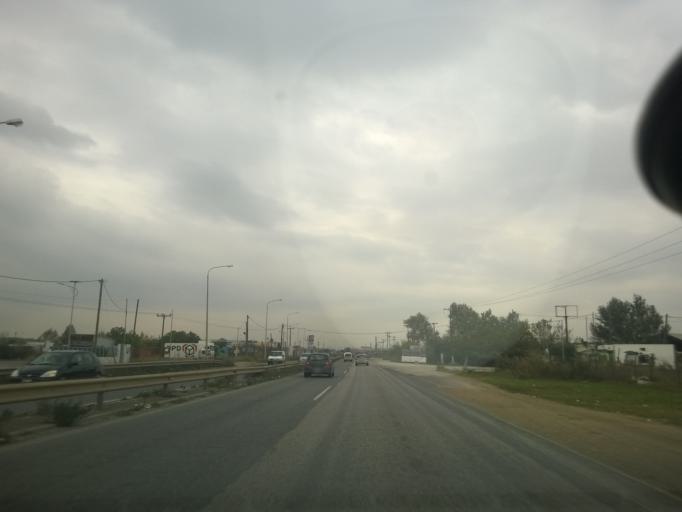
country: GR
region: Central Macedonia
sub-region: Nomos Thessalonikis
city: Sindos
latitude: 40.7059
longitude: 22.8047
